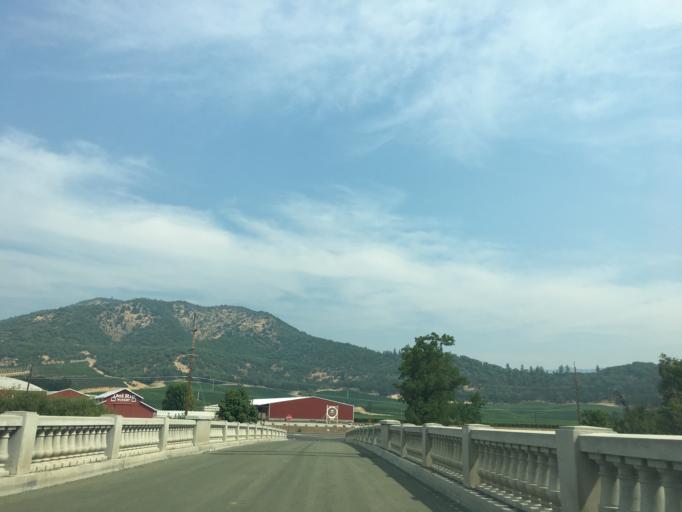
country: US
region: Oregon
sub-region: Jackson County
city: Gold Hill
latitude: 42.4323
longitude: -123.0905
